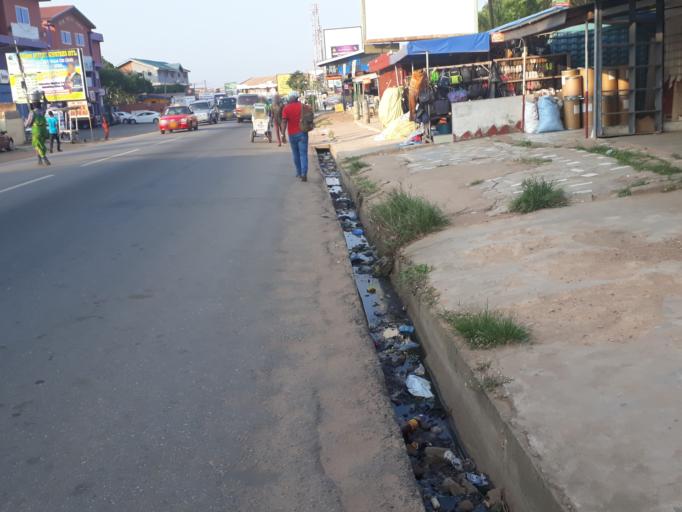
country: GH
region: Greater Accra
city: Dome
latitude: 5.6409
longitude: -0.2400
